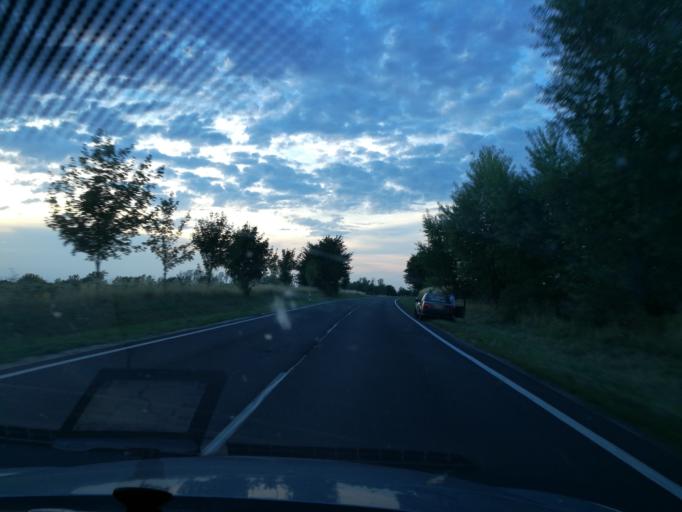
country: HU
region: Komarom-Esztergom
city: Kisber
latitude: 47.4929
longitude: 18.0506
